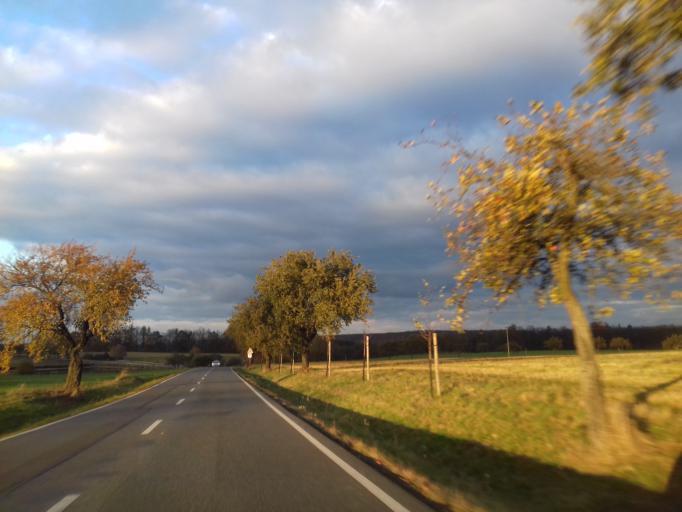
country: CZ
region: Pardubicky
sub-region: Okres Chrudim
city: Skutec
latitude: 49.8236
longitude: 16.0420
